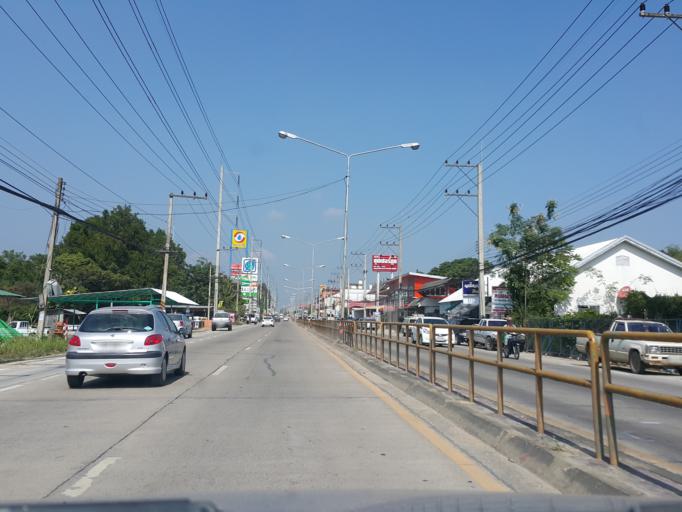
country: TH
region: Chiang Mai
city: San Sai
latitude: 18.8992
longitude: 98.9510
